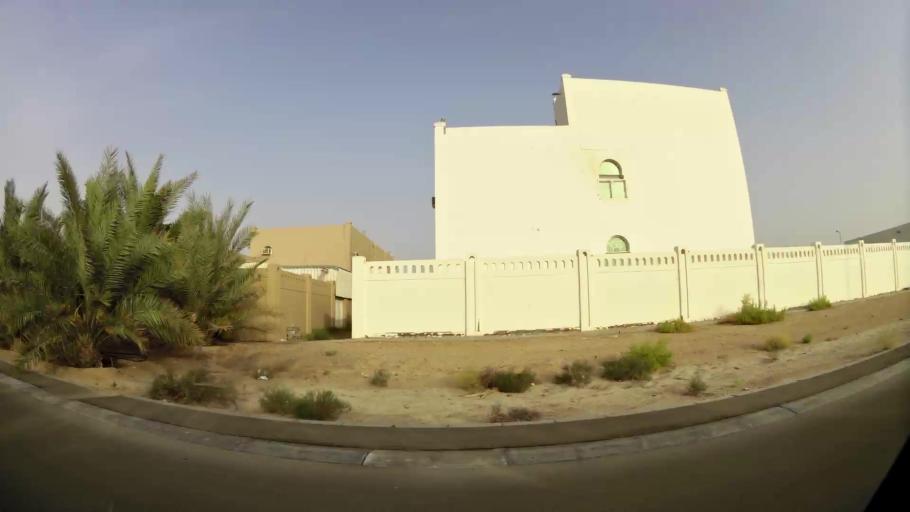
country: AE
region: Abu Dhabi
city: Al Ain
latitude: 24.1094
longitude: 55.7087
